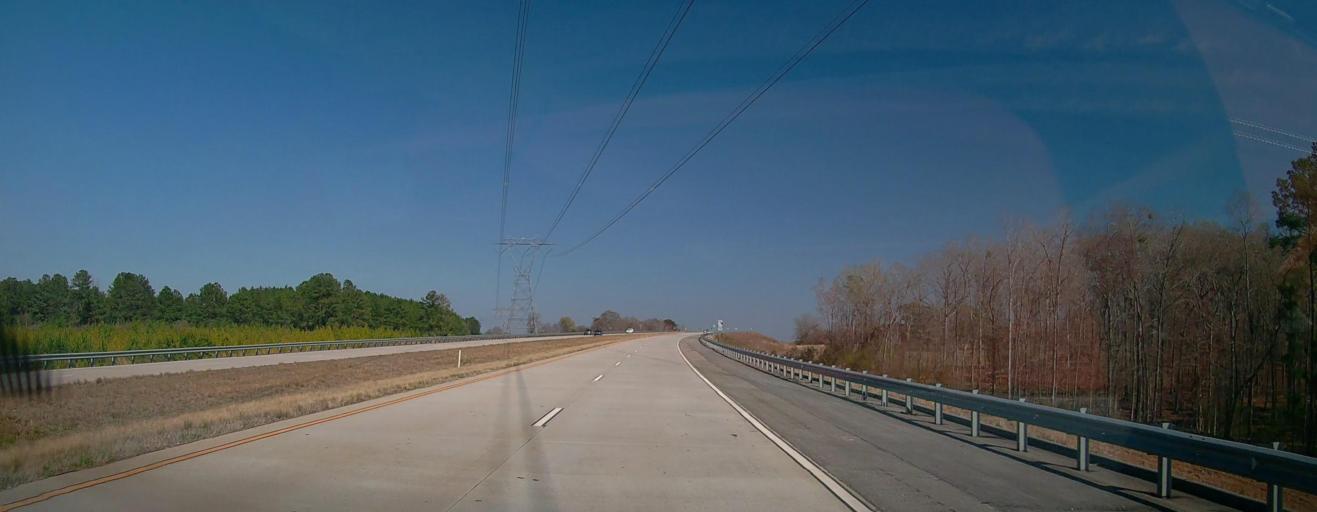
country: US
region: Georgia
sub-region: Jones County
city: Gray
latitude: 33.0272
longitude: -83.5452
